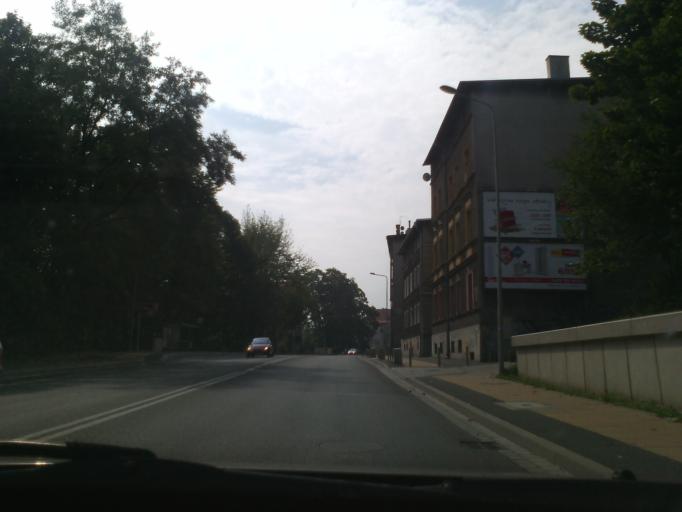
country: PL
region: Lower Silesian Voivodeship
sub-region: Powiat walbrzyski
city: Walbrzych
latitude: 50.7914
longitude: 16.2874
